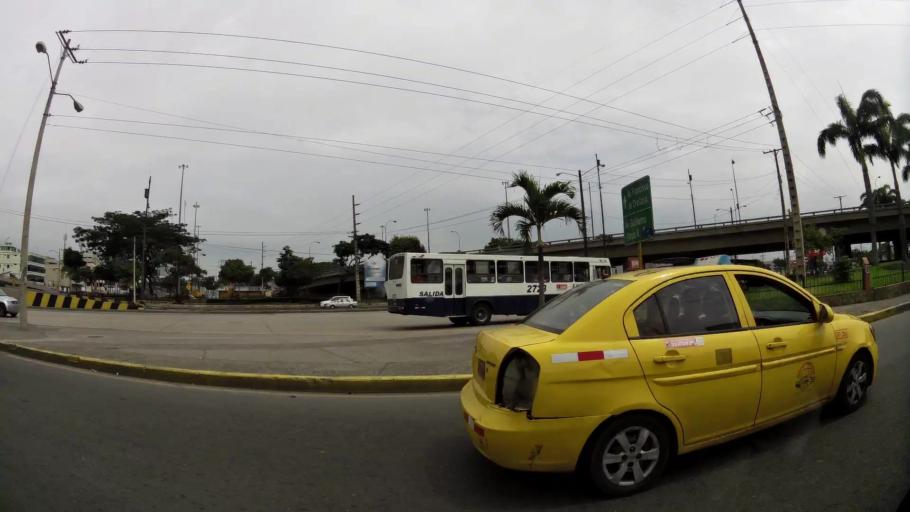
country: EC
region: Guayas
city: Eloy Alfaro
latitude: -2.1551
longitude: -79.8949
